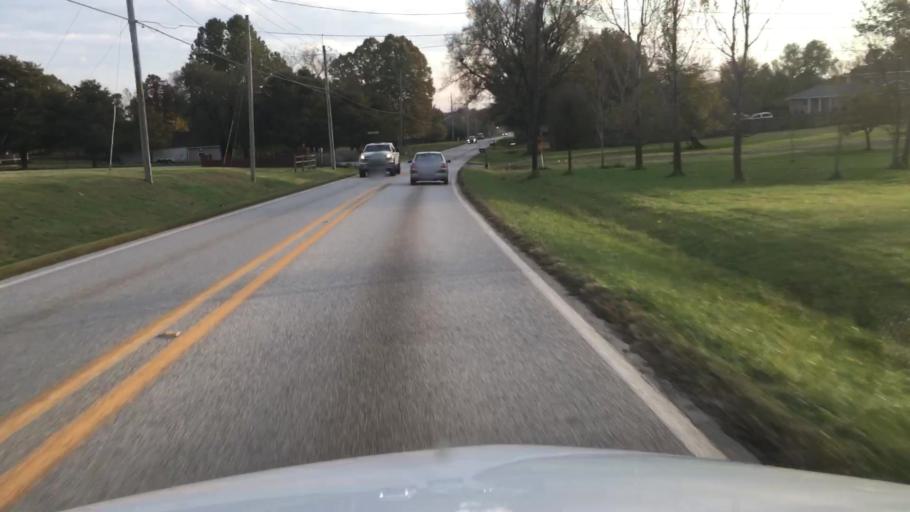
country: US
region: Arkansas
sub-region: Washington County
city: Elm Springs
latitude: 36.2174
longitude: -94.2308
